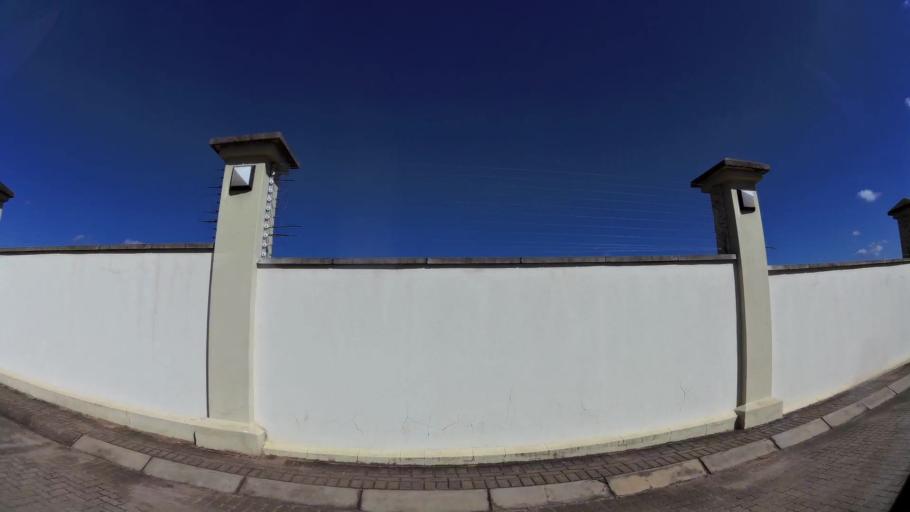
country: ZA
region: Limpopo
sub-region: Mopani District Municipality
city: Tzaneen
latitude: -23.8168
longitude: 30.1692
